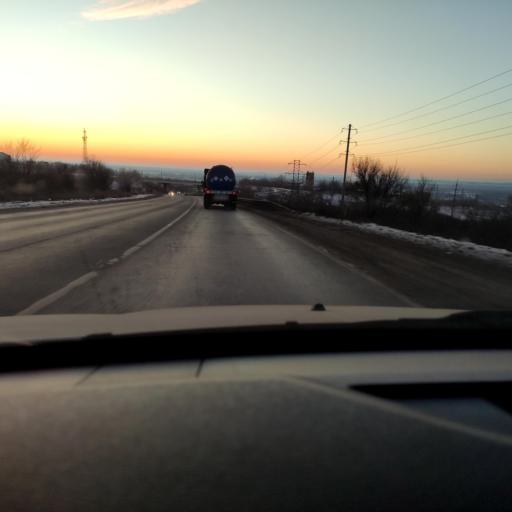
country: RU
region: Samara
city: Smyshlyayevka
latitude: 53.2441
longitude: 50.4771
